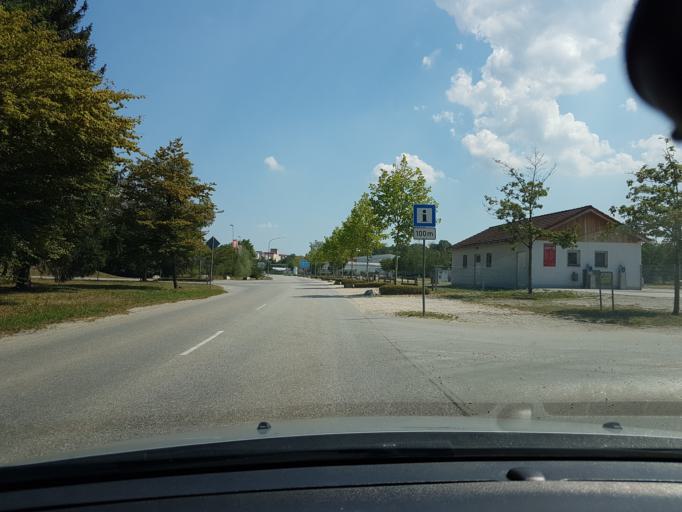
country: DE
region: Bavaria
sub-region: Upper Bavaria
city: Neuotting
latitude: 48.2403
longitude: 12.6754
